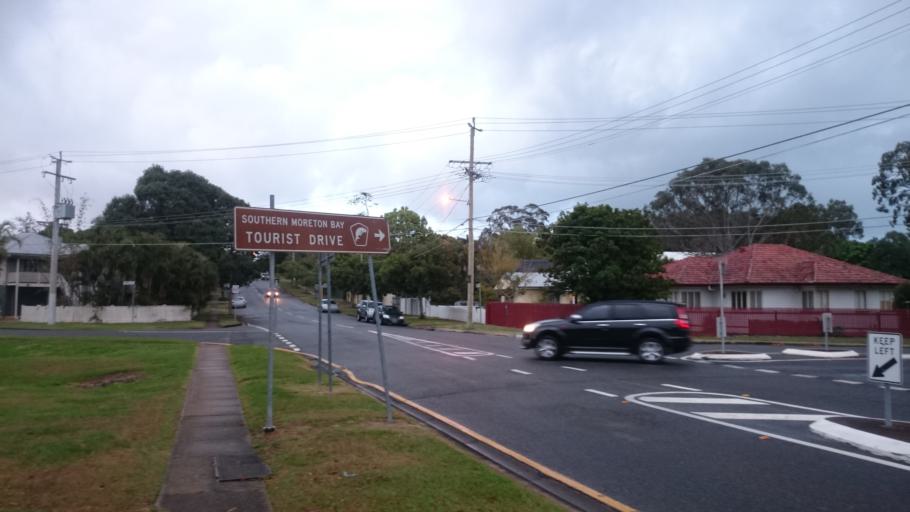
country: AU
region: Queensland
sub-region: Brisbane
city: Manly West
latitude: -27.4671
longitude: 153.1821
